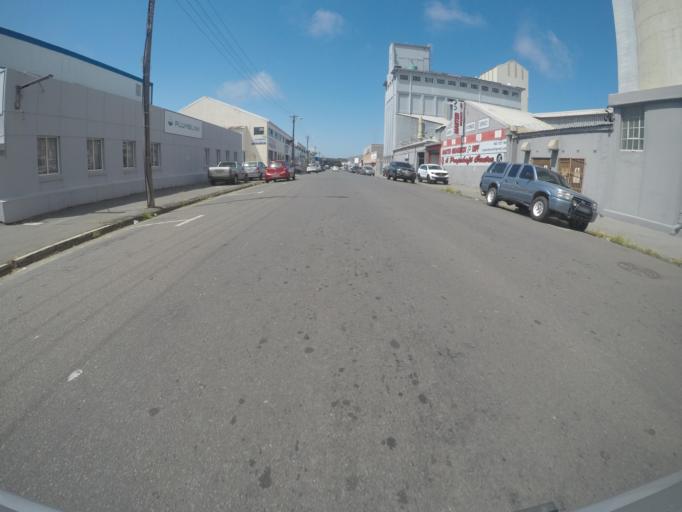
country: ZA
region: Eastern Cape
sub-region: Buffalo City Metropolitan Municipality
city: East London
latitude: -33.0094
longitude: 27.9079
